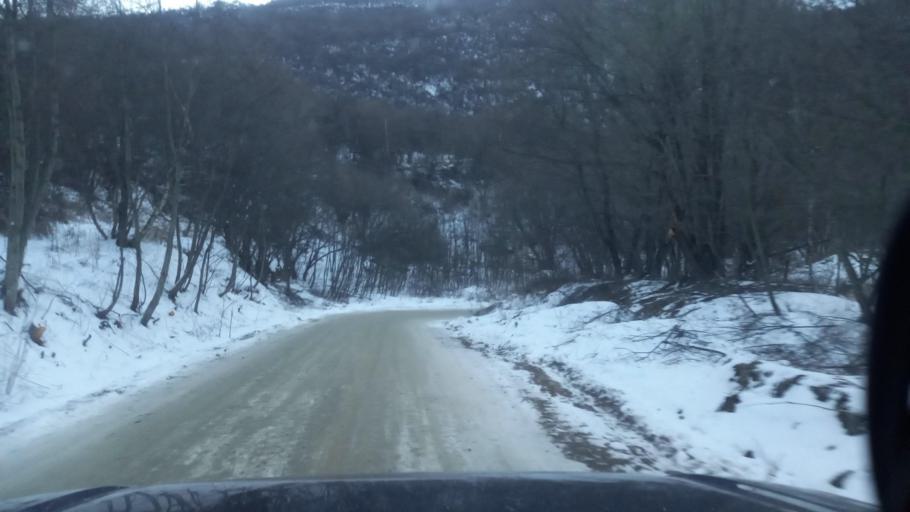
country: RU
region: Ingushetiya
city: Dzhayrakh
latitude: 42.8284
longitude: 44.5814
